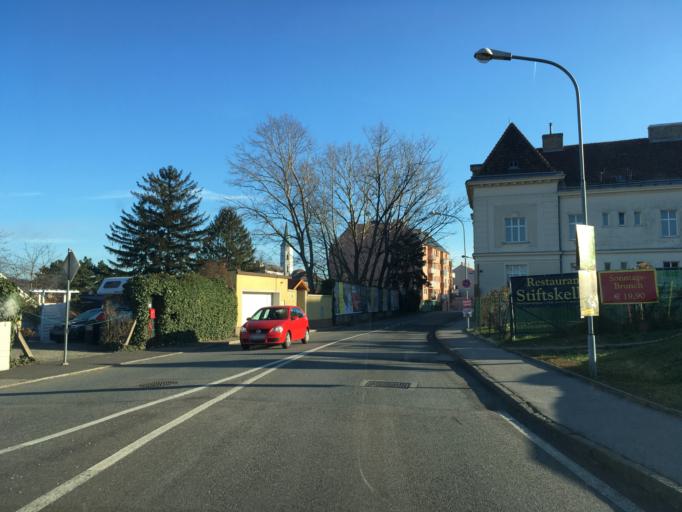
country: AT
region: Lower Austria
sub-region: Politischer Bezirk Wien-Umgebung
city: Klosterneuburg
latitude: 48.3156
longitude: 16.3147
